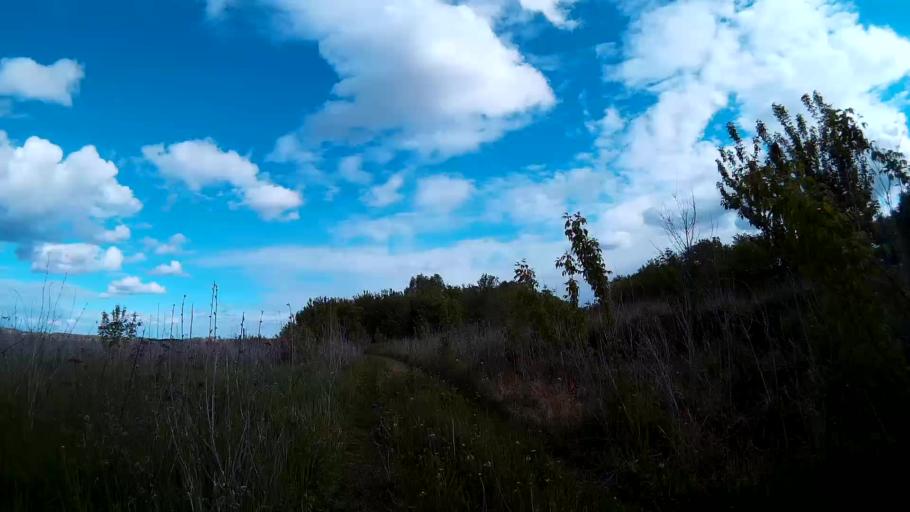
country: RU
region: Ulyanovsk
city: Novoul'yanovsk
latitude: 54.2171
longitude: 48.2582
